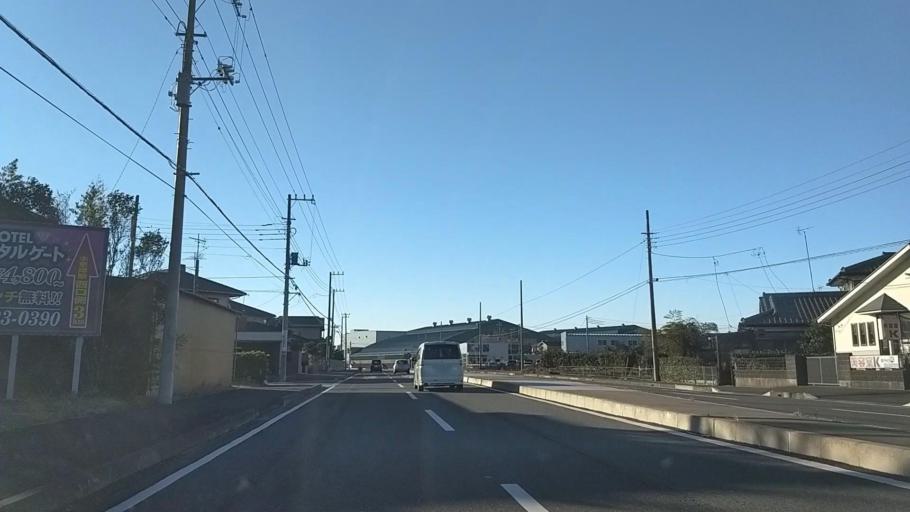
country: JP
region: Chiba
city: Kisarazu
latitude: 35.4074
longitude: 139.9185
